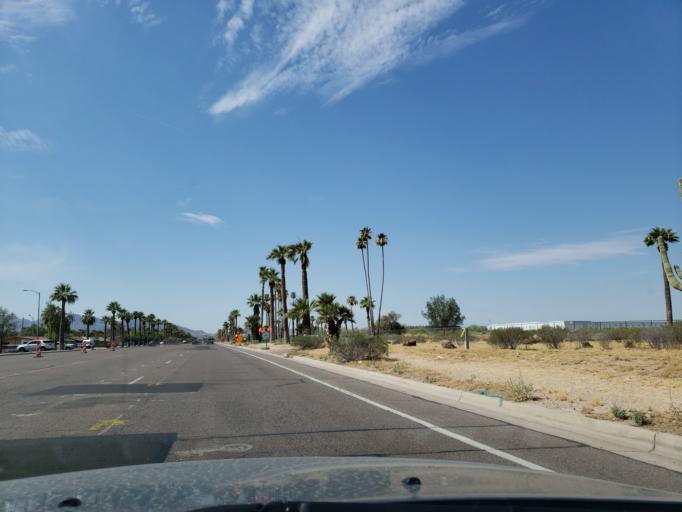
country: US
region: Arizona
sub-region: Maricopa County
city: Goodyear
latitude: 33.4474
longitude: -112.3583
